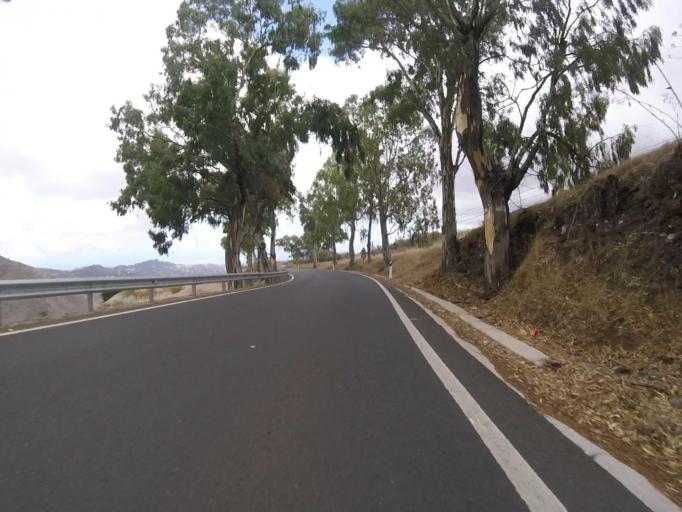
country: ES
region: Canary Islands
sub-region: Provincia de Las Palmas
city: Vega de San Mateo
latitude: 28.0027
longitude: -15.5626
